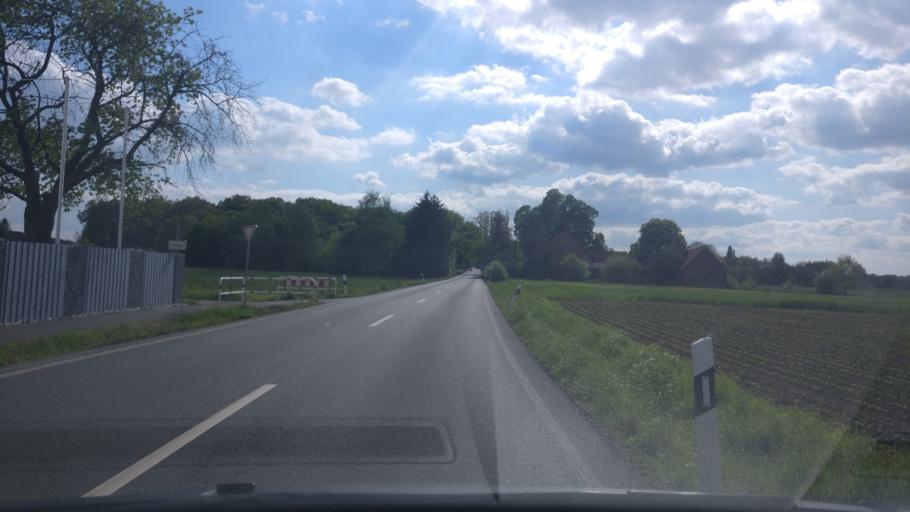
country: DE
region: North Rhine-Westphalia
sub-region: Regierungsbezirk Detmold
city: Leopoldshohe
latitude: 52.0044
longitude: 8.7382
